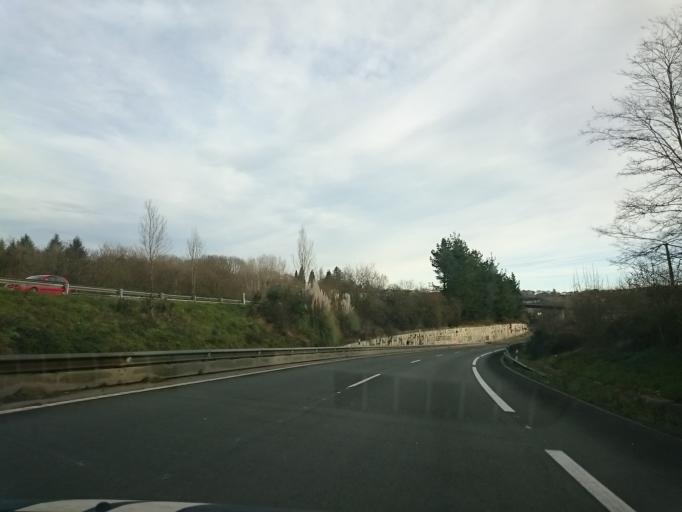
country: ES
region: Asturias
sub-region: Province of Asturias
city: Oviedo
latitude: 43.3290
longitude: -5.8737
